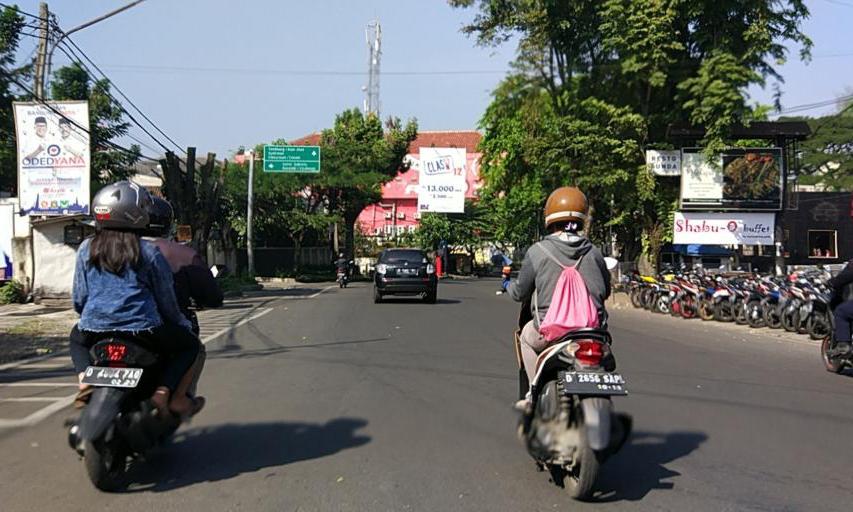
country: ID
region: West Java
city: Bandung
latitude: -6.9170
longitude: 107.6137
